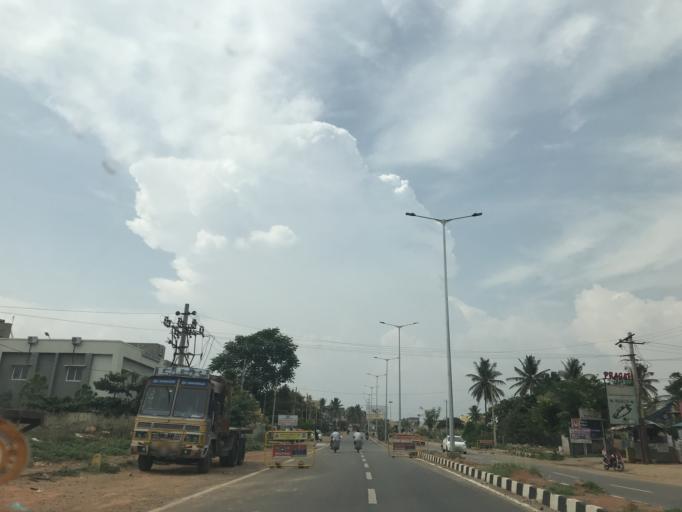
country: IN
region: Karnataka
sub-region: Bangalore Urban
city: Yelahanka
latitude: 13.1393
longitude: 77.6705
